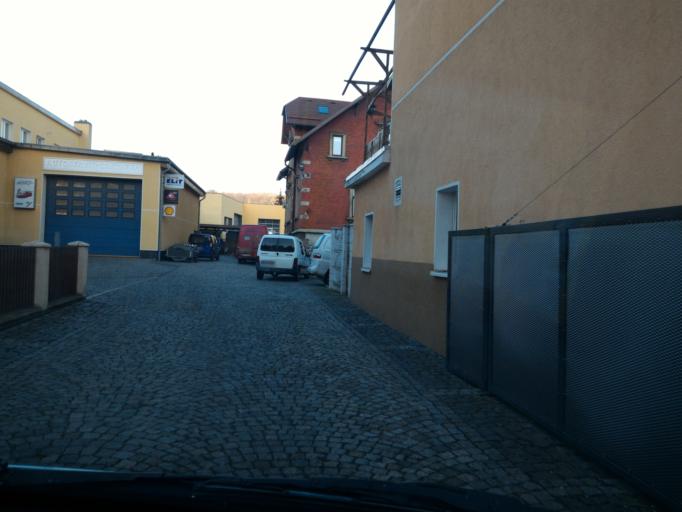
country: CZ
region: Ustecky
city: Varnsdorf
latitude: 50.9117
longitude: 14.6320
